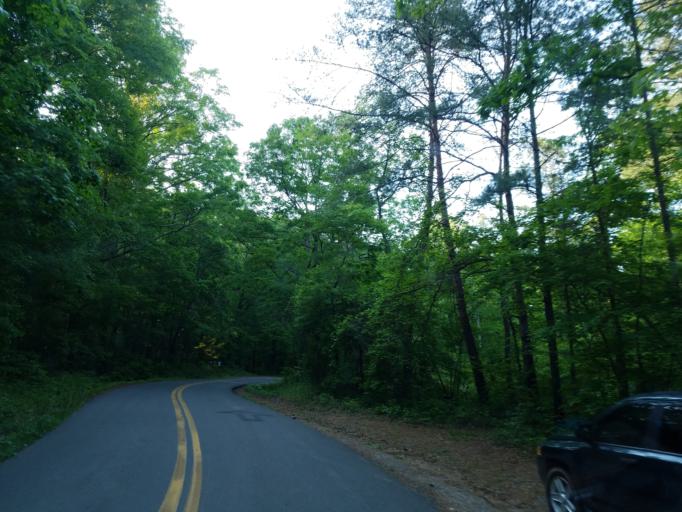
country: US
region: Georgia
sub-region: Gordon County
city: Calhoun
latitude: 34.5641
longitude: -85.1014
